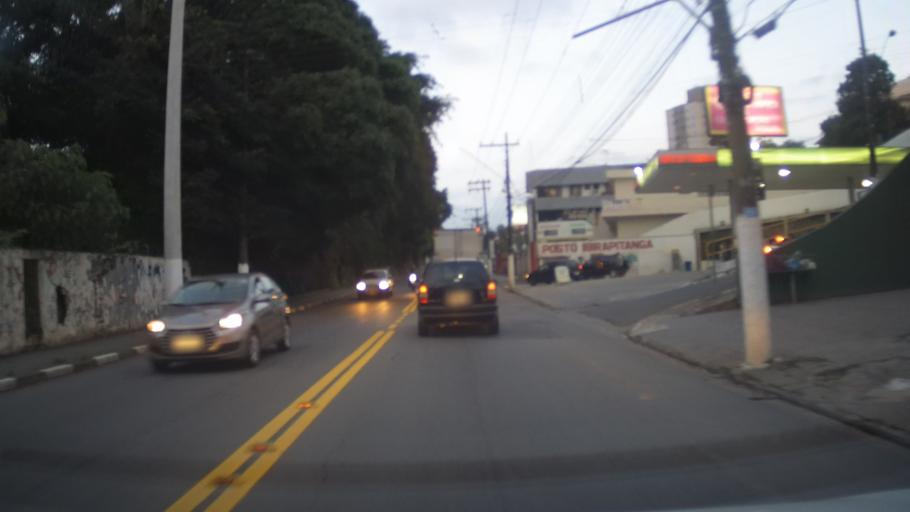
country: BR
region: Sao Paulo
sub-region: Aruja
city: Aruja
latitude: -23.3910
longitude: -46.3172
